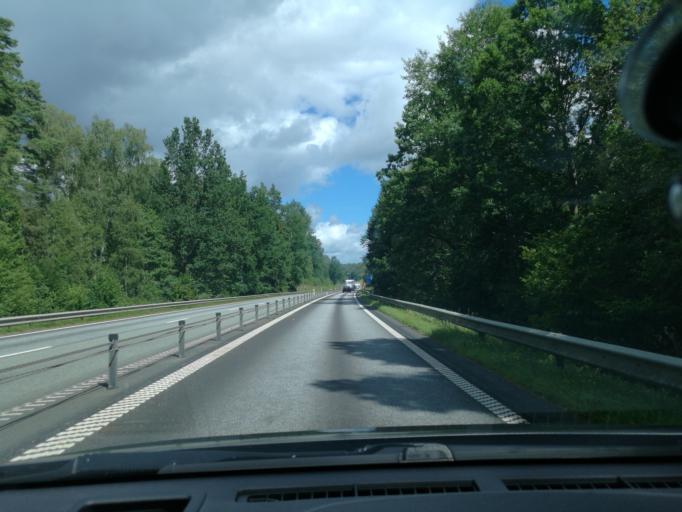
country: SE
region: Skane
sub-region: Osby Kommun
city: Osby
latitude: 56.3631
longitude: 14.0188
